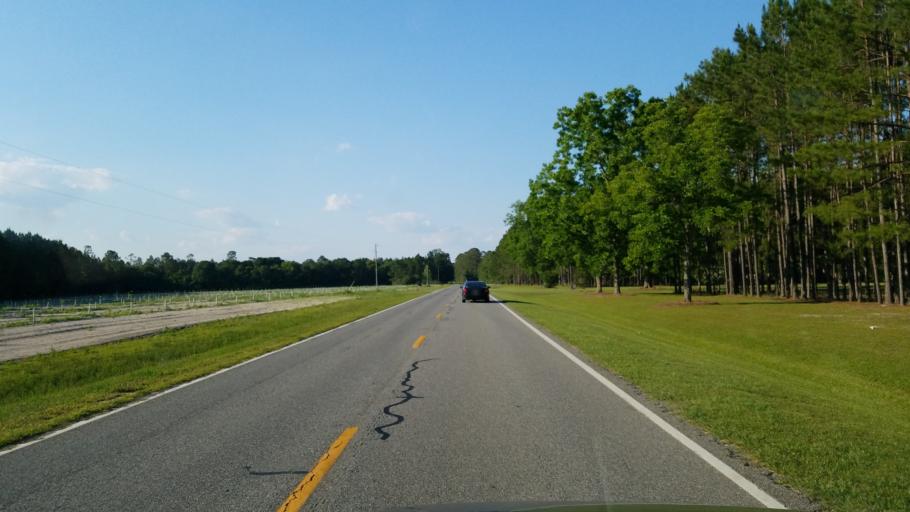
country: US
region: Georgia
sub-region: Lanier County
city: Lakeland
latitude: 30.9871
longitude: -83.0718
